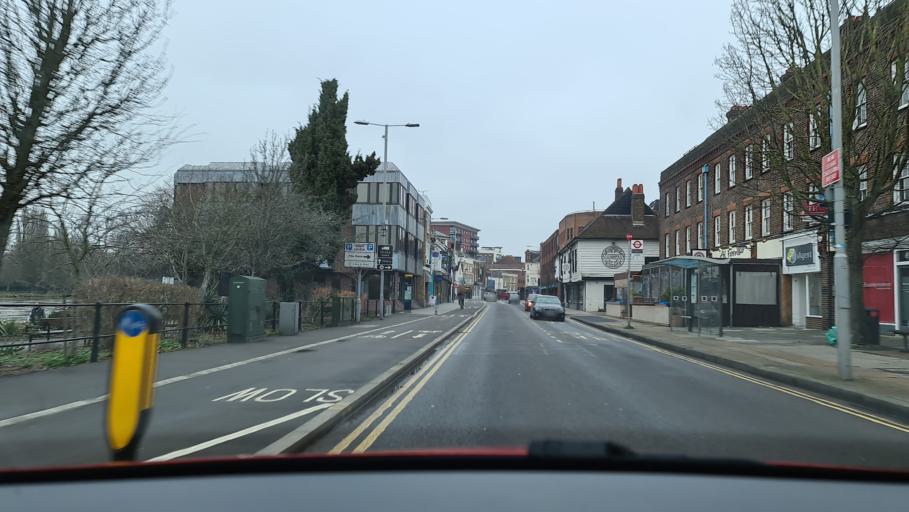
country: GB
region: England
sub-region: Greater London
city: Kingston upon Thames
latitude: 51.4063
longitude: -0.3081
